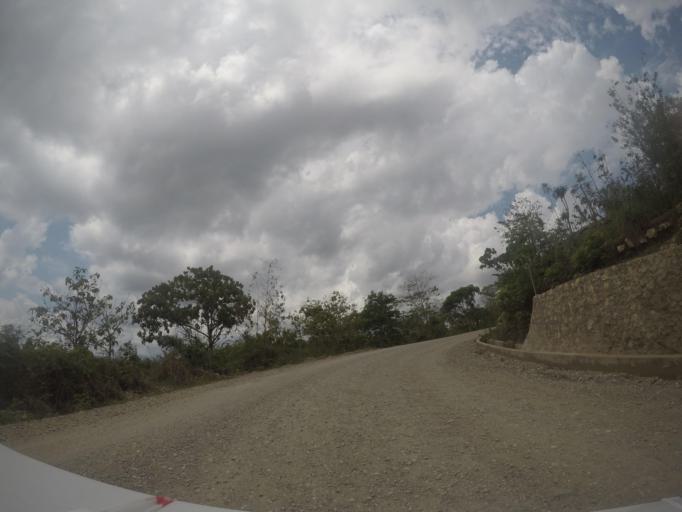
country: TL
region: Baucau
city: Baucau
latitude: -8.5349
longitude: 126.4245
